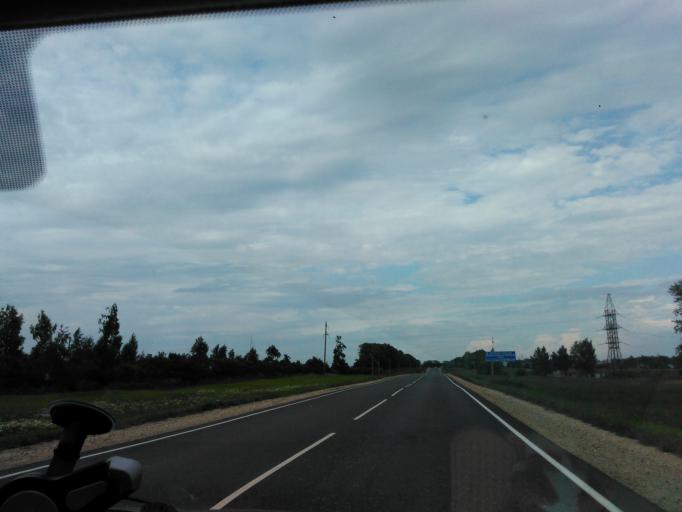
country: RU
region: Penza
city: Lermontovo
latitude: 52.9913
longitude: 43.6397
